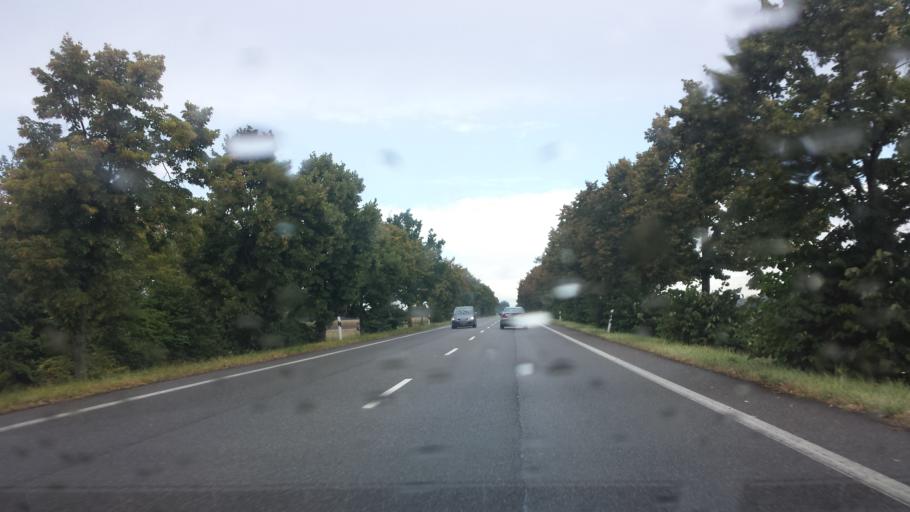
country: DE
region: Rheinland-Pfalz
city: Bobenheim-Roxheim
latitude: 49.5988
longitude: 8.3574
